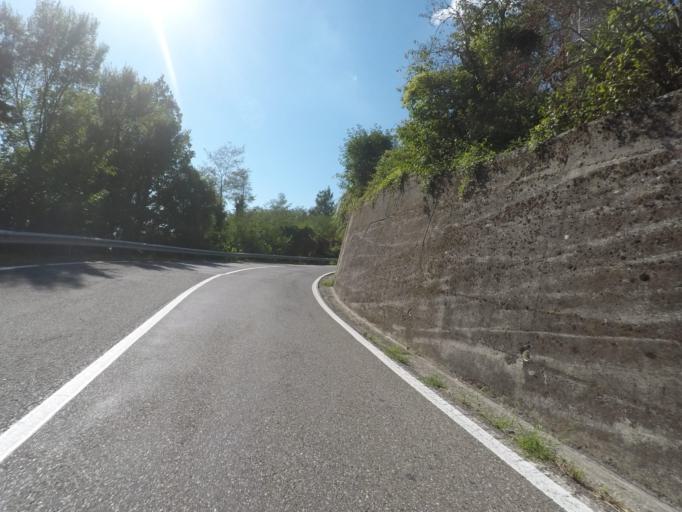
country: IT
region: Tuscany
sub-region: Provincia di Massa-Carrara
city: Casola in Lunigiana
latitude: 44.2500
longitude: 10.1780
